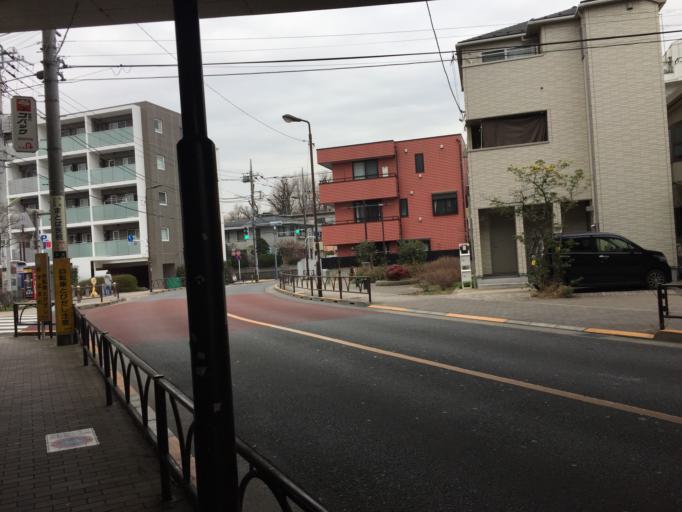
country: JP
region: Tokyo
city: Tokyo
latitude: 35.6563
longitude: 139.6548
